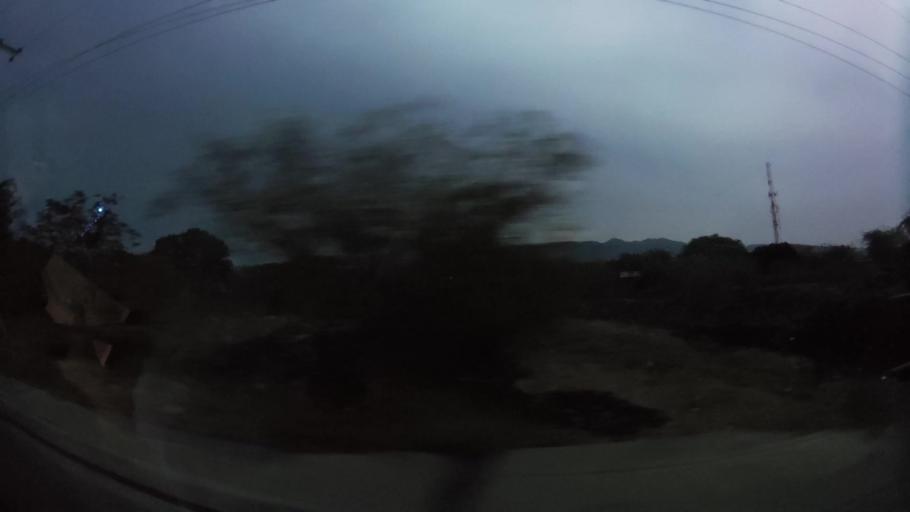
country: NI
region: Esteli
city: Esteli
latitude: 13.0997
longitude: -86.3571
